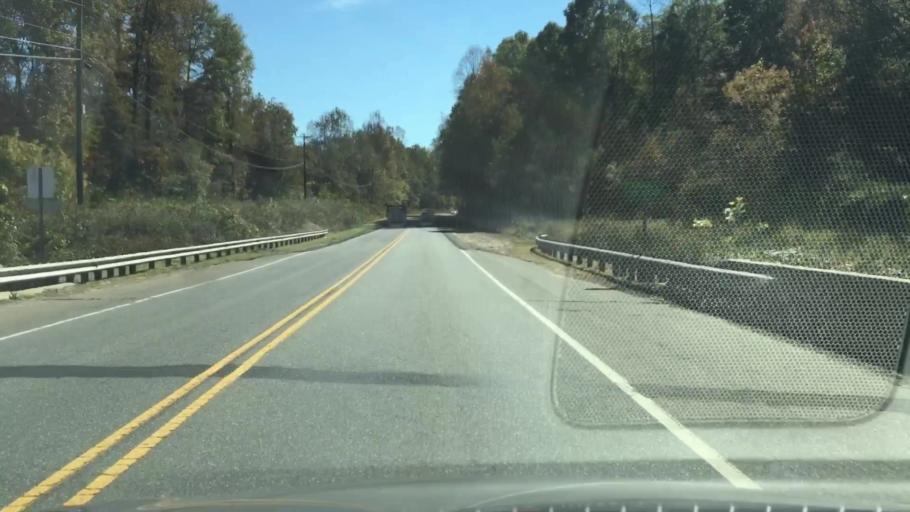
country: US
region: North Carolina
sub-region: Rockingham County
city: Reidsville
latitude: 36.2767
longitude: -79.6498
